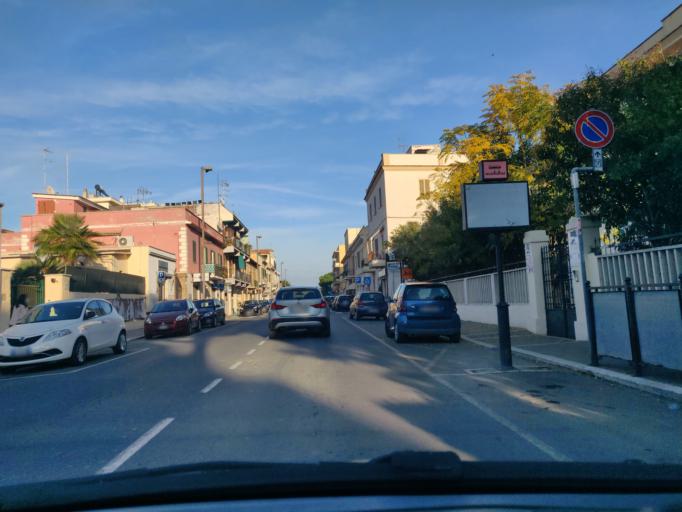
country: IT
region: Latium
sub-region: Citta metropolitana di Roma Capitale
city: Santa Marinella
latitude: 42.0356
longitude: 11.8664
